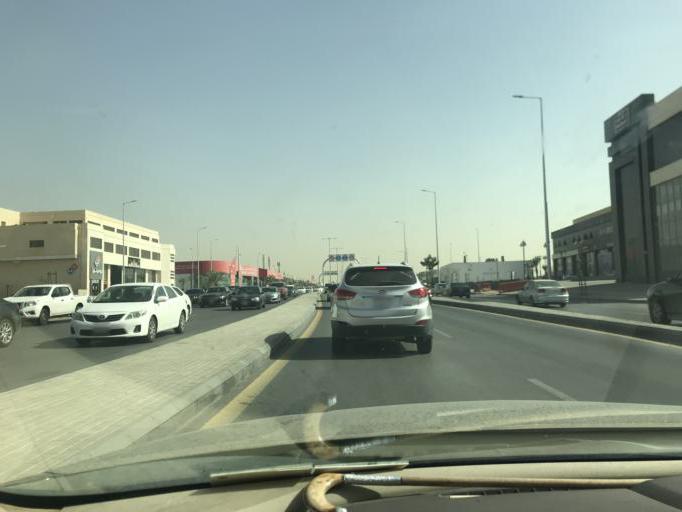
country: SA
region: Ar Riyad
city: Riyadh
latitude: 24.7853
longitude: 46.7476
